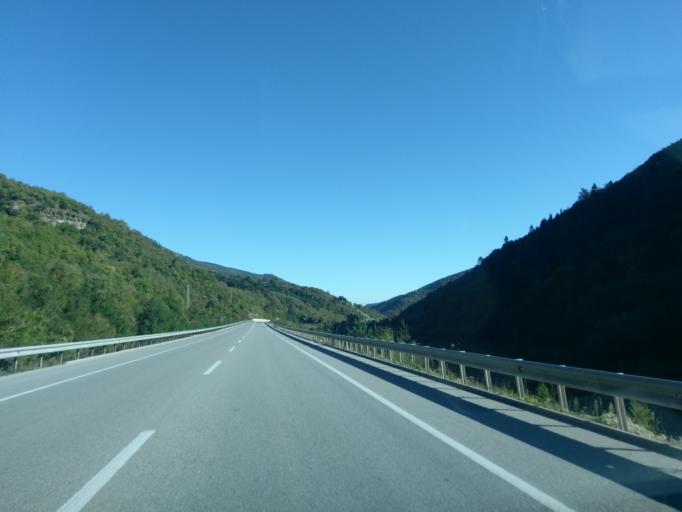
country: TR
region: Sinop
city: Erfelek
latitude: 41.7188
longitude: 34.9366
